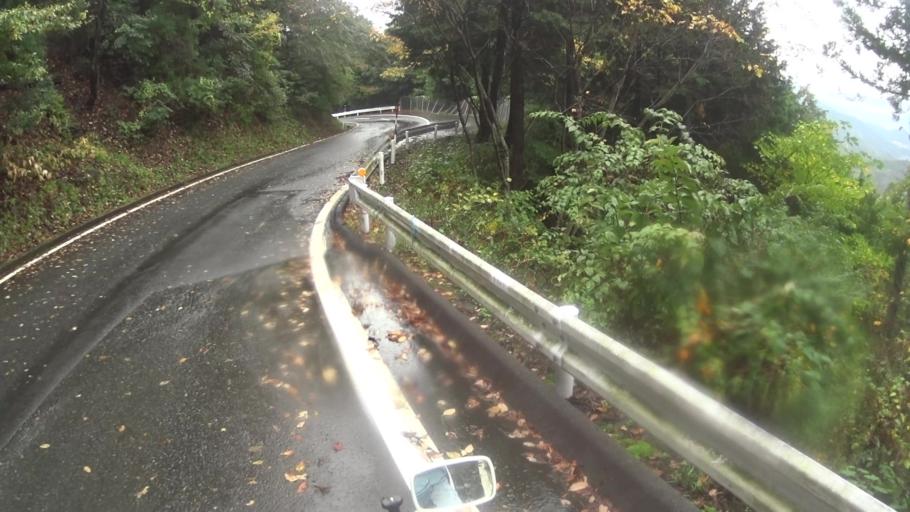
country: JP
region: Kyoto
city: Miyazu
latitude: 35.4808
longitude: 135.1583
